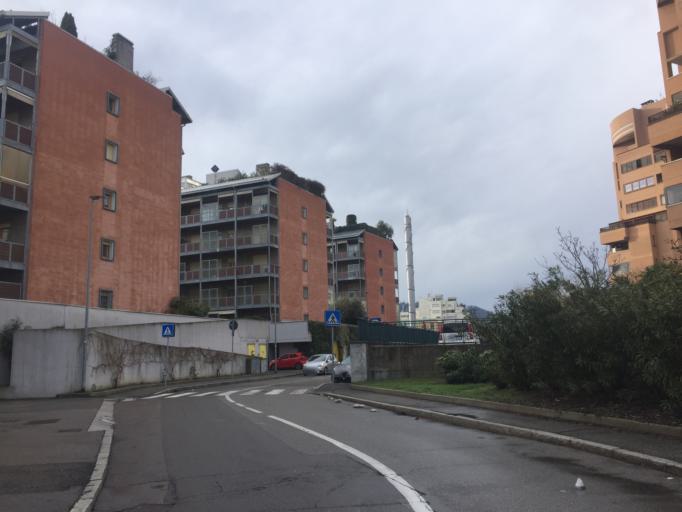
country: IT
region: Emilia-Romagna
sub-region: Provincia di Bologna
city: Bologna
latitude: 44.5051
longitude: 11.3043
